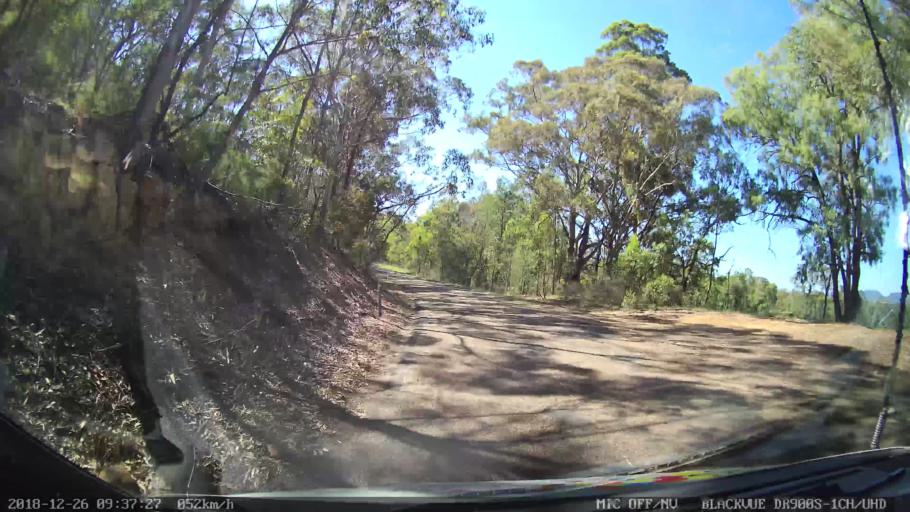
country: AU
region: New South Wales
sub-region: Mid-Western Regional
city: Kandos
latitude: -32.9325
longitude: 150.0403
